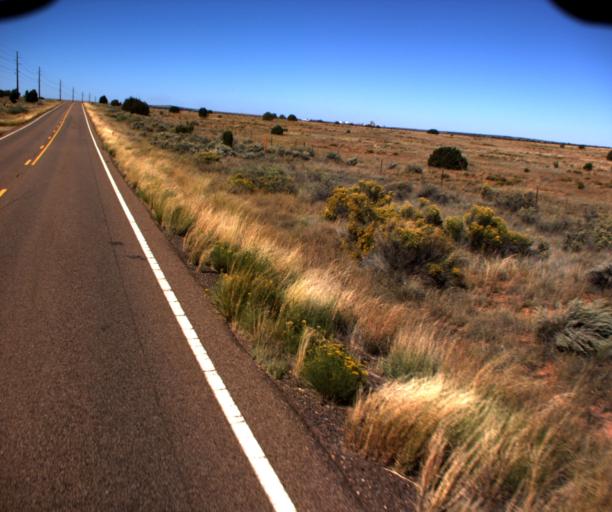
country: US
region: Arizona
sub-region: Navajo County
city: Taylor
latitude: 34.4838
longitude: -110.2611
